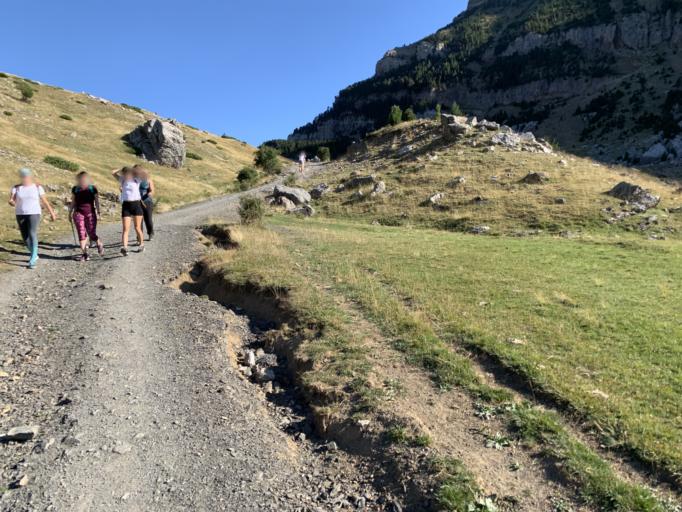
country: ES
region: Aragon
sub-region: Provincia de Huesca
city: Hoz de Jaca
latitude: 42.6964
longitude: -0.3536
